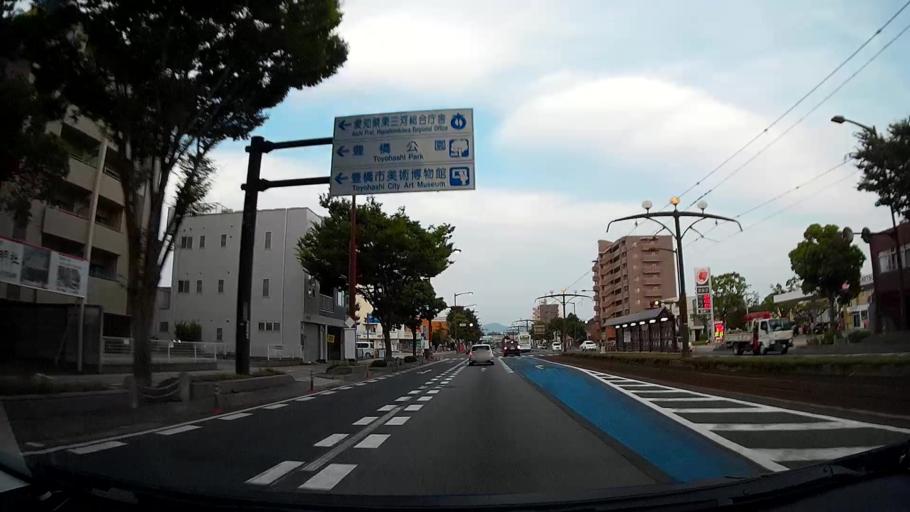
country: JP
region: Aichi
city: Toyohashi
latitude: 34.7671
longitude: 137.3943
